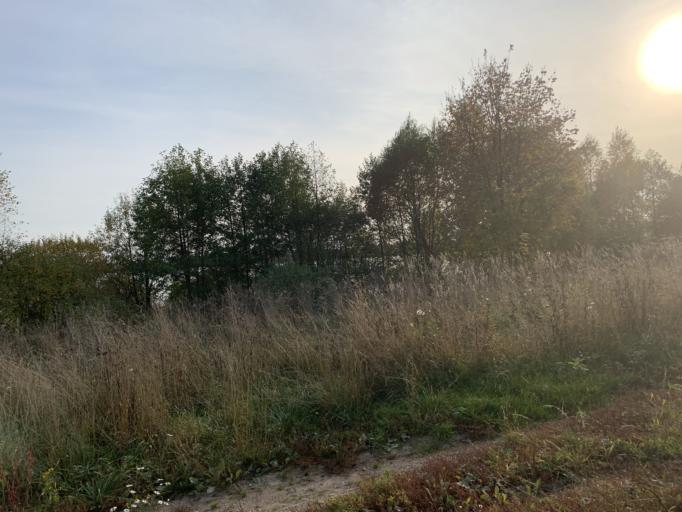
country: RU
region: Jaroslavl
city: Porech'ye-Rybnoye
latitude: 56.9785
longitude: 39.3854
